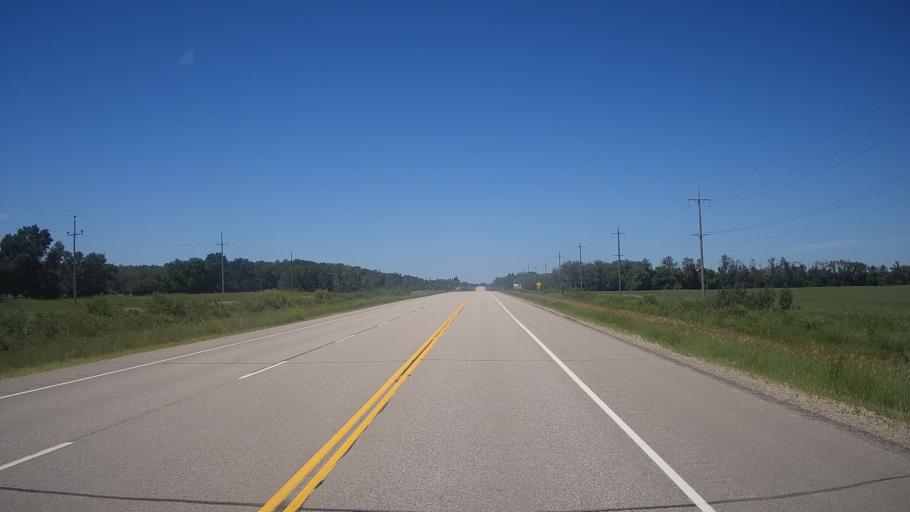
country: CA
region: Manitoba
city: Neepawa
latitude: 50.2253
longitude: -99.3457
